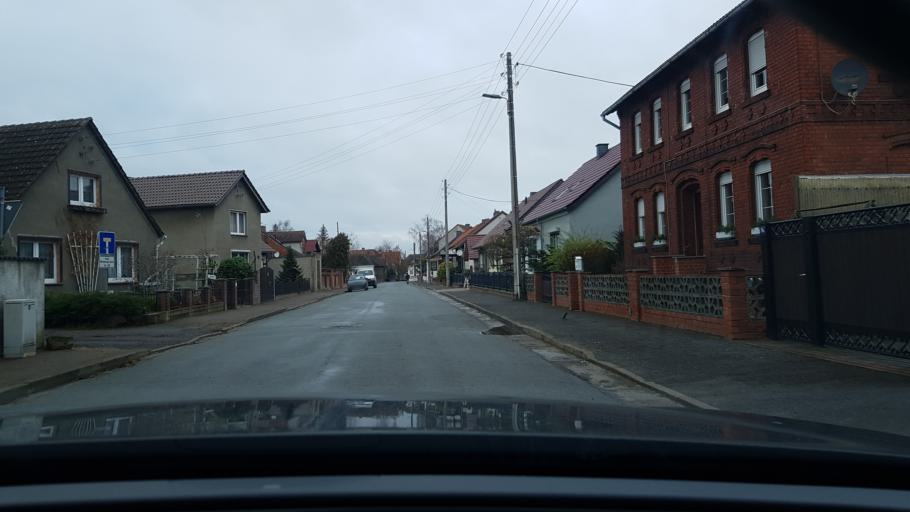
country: DE
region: Saxony-Anhalt
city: Weferlingen
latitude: 52.3985
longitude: 11.1153
